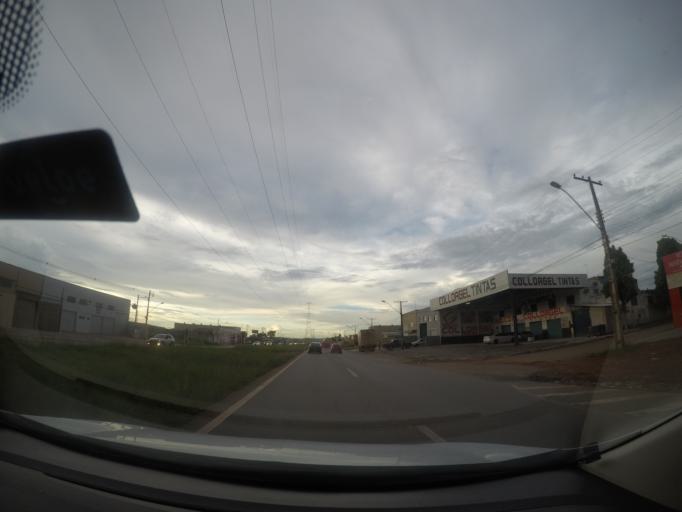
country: BR
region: Goias
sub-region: Goiania
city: Goiania
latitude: -16.7417
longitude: -49.3448
